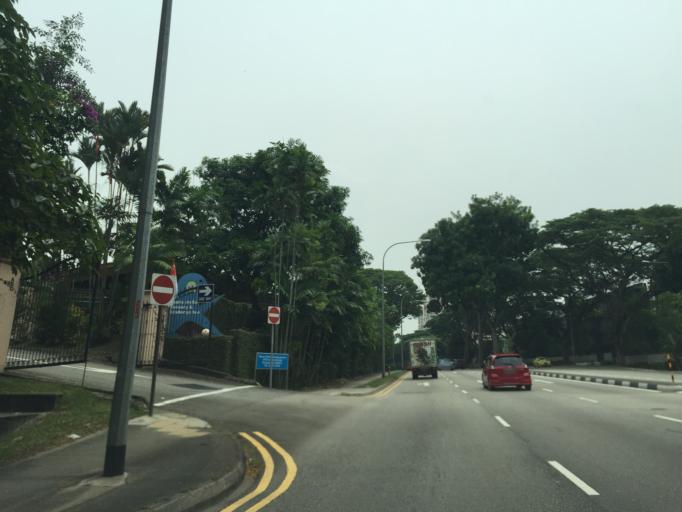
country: SG
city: Singapore
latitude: 1.3086
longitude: 103.8092
